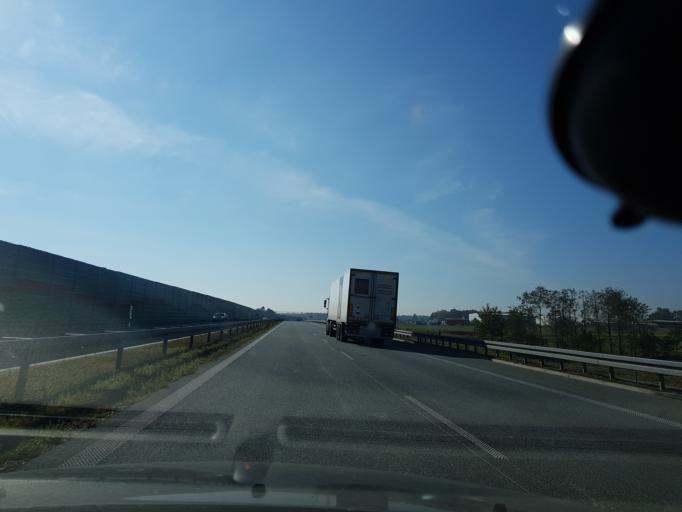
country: PL
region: Lodz Voivodeship
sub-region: Powiat tomaszowski
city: Lubochnia
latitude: 51.6024
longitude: 20.0590
